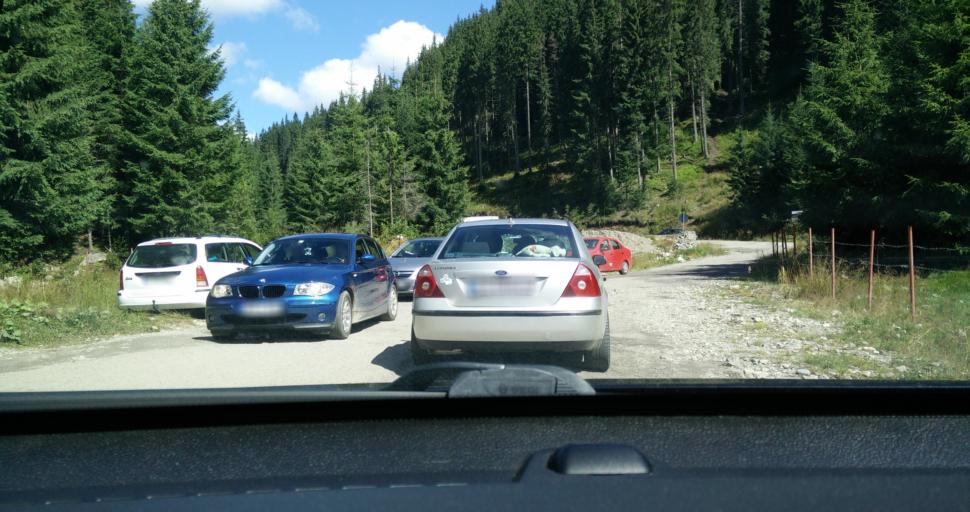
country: RO
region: Hunedoara
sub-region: Oras Petrila
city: Petrila
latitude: 45.4378
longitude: 23.6293
